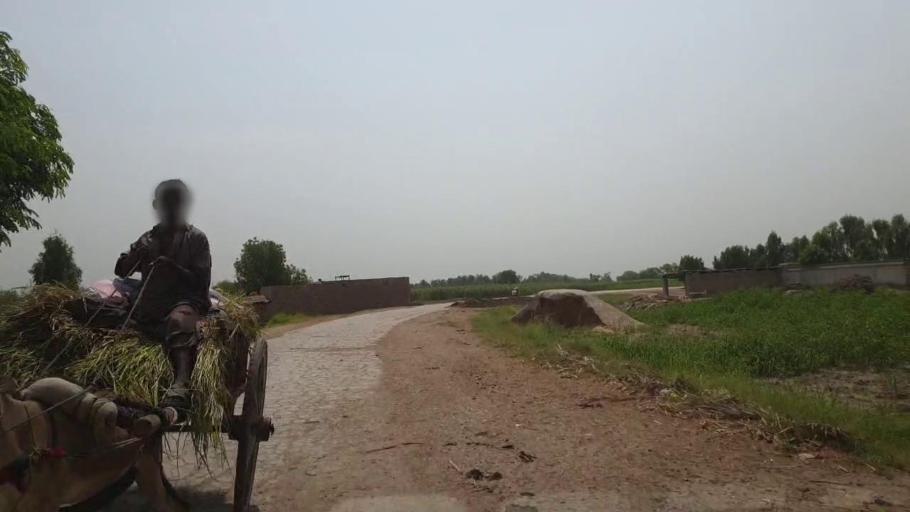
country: PK
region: Sindh
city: Gambat
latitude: 27.4449
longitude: 68.5141
